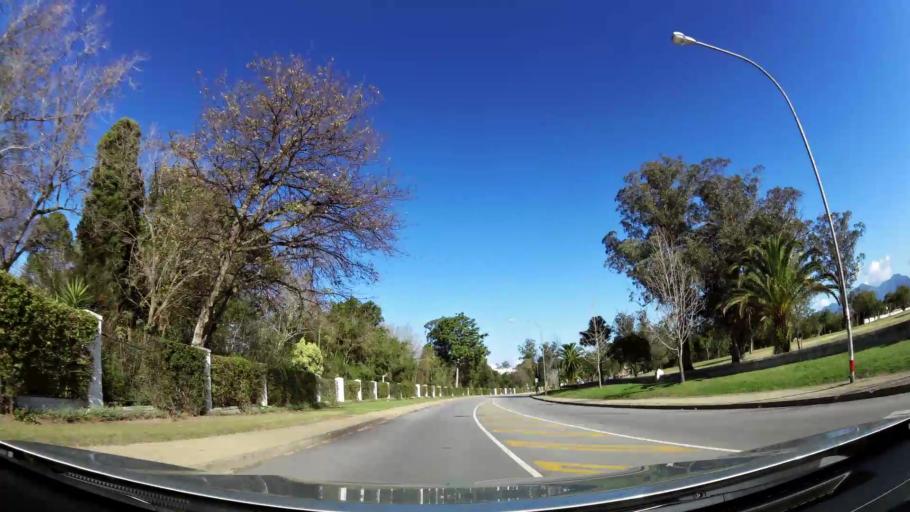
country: ZA
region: Western Cape
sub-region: Eden District Municipality
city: George
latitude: -33.9515
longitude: 22.4056
